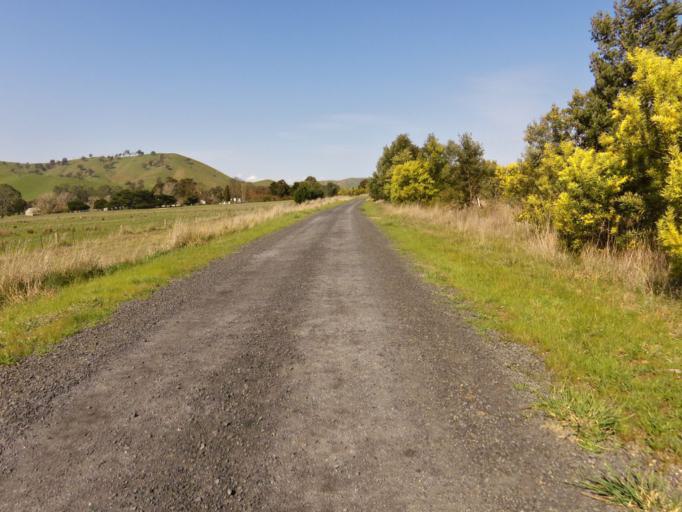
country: AU
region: Victoria
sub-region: Murrindindi
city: Alexandra
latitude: -37.0160
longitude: 145.7938
